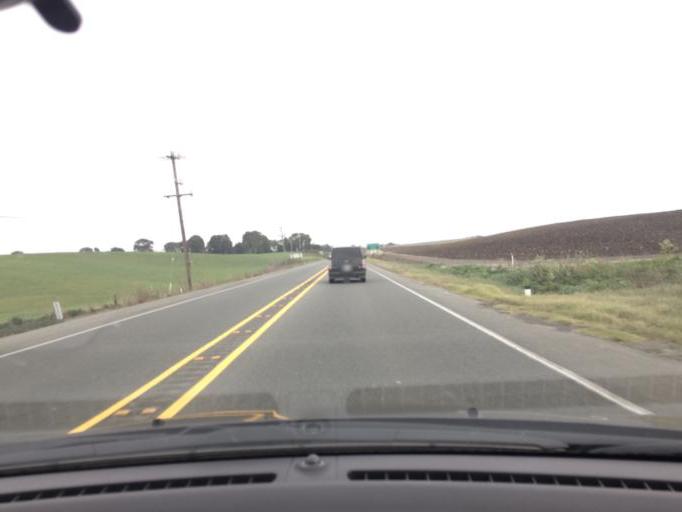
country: US
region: California
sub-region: Monterey County
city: Castroville
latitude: 36.7698
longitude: -121.7387
